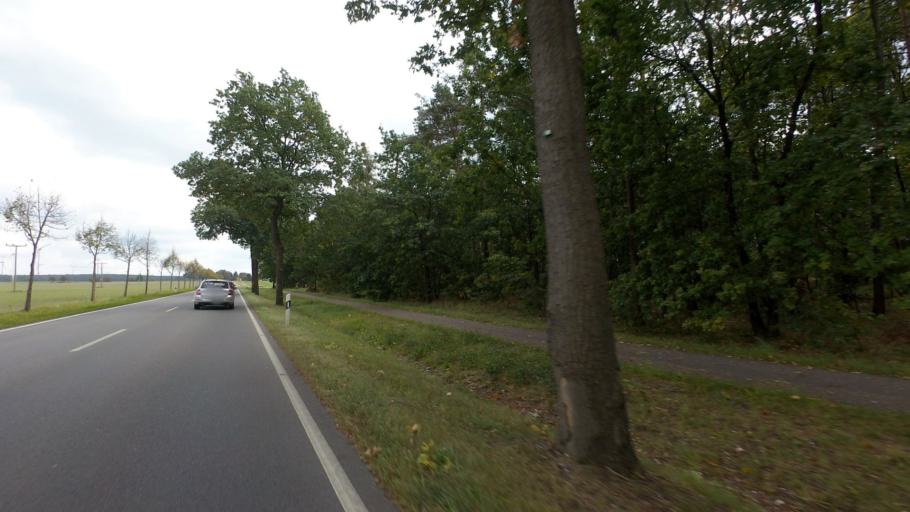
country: DE
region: Brandenburg
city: Finsterwalde
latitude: 51.6344
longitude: 13.7555
